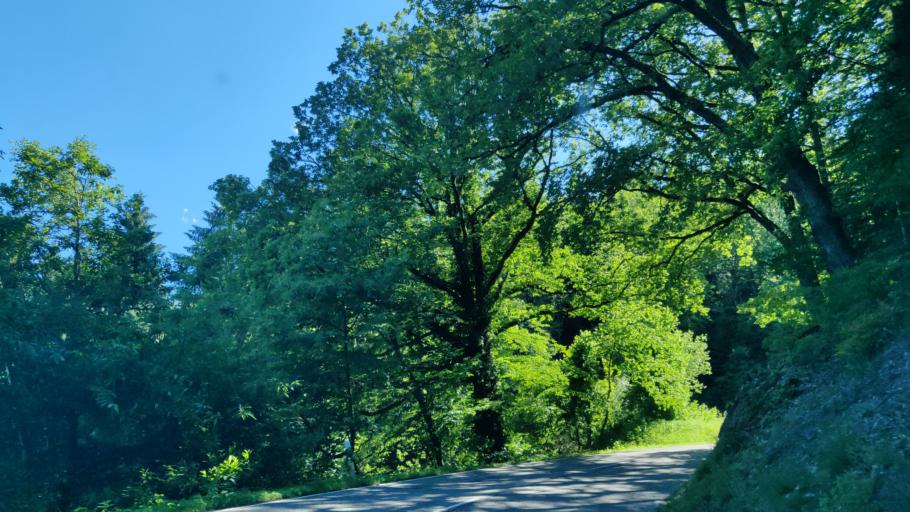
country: DE
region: Baden-Wuerttemberg
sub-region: Karlsruhe Region
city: Gernsbach
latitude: 48.7599
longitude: 8.3201
